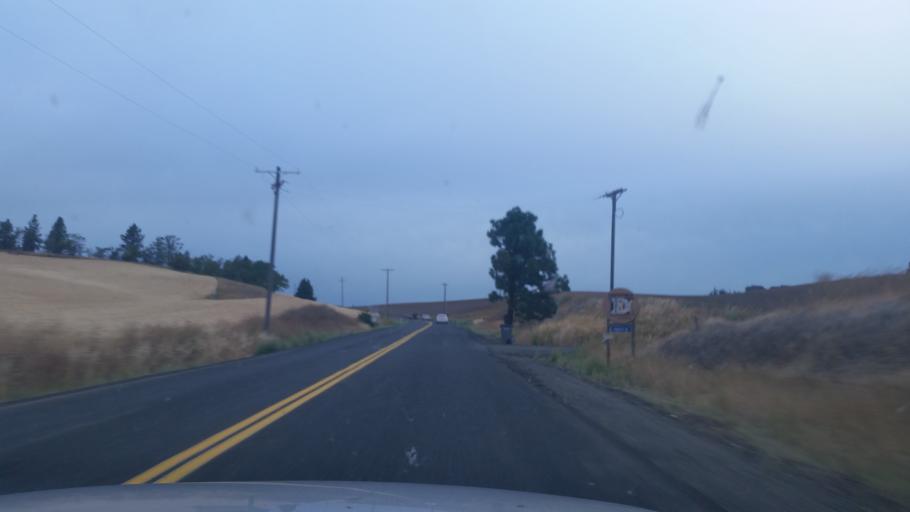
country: US
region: Washington
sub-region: Spokane County
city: Cheney
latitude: 47.5149
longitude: -117.5925
